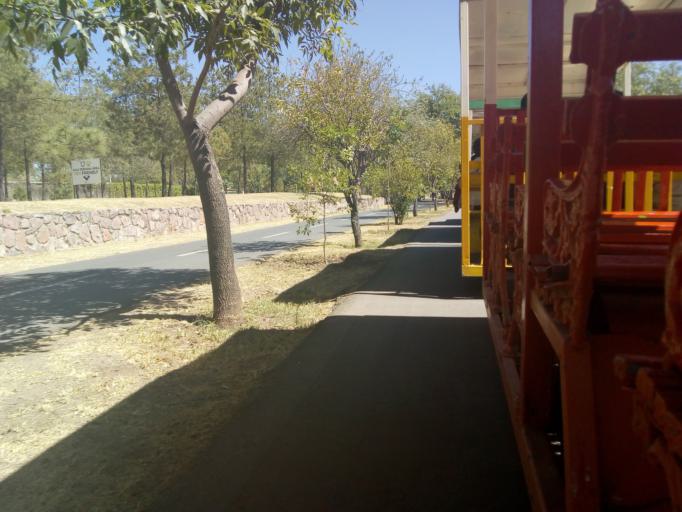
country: MX
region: Guanajuato
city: Leon
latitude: 21.1867
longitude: -101.6794
